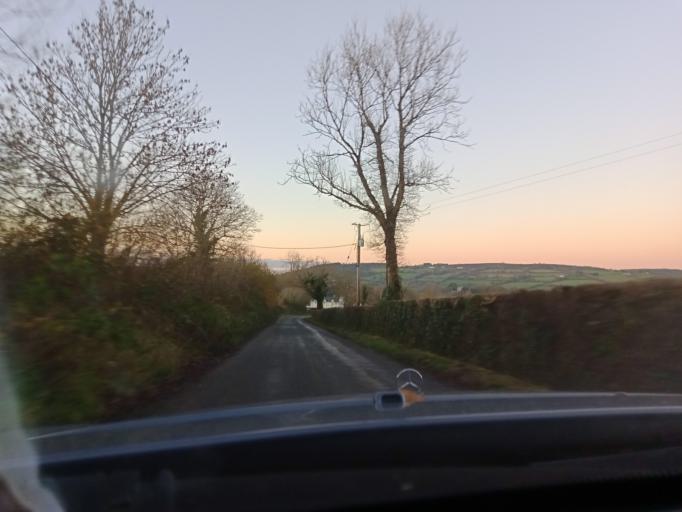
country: IE
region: Leinster
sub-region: Kilkenny
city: Thomastown
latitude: 52.4860
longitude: -7.1017
